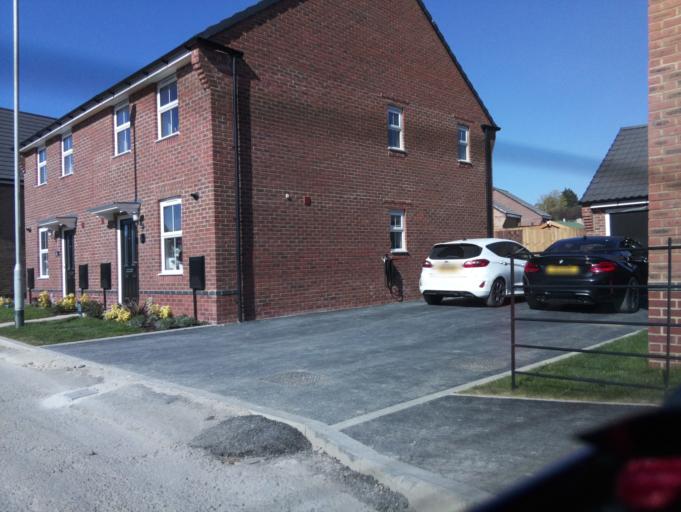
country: GB
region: England
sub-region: Gloucestershire
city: Stonehouse
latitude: 51.7572
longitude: -2.3115
